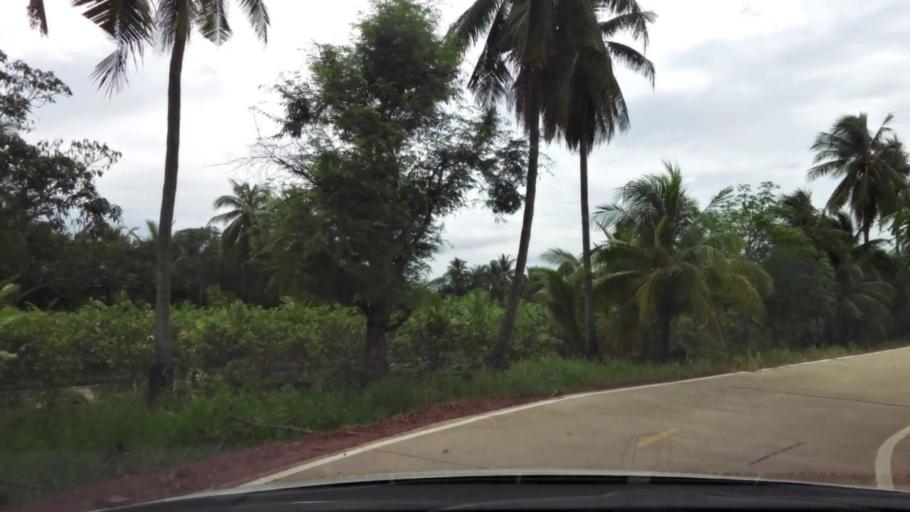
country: TH
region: Ratchaburi
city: Damnoen Saduak
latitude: 13.5573
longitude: 99.9801
